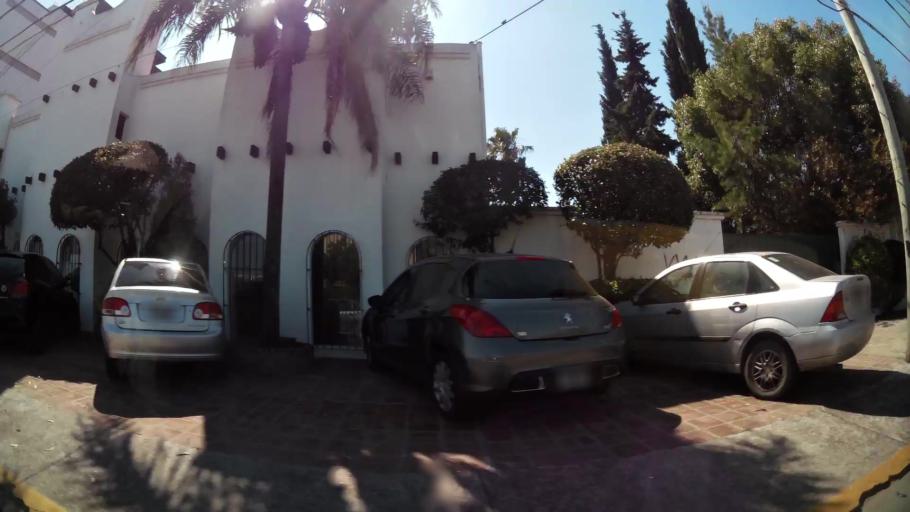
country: AR
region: Buenos Aires
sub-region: Partido de Tigre
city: Tigre
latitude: -34.4293
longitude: -58.5840
